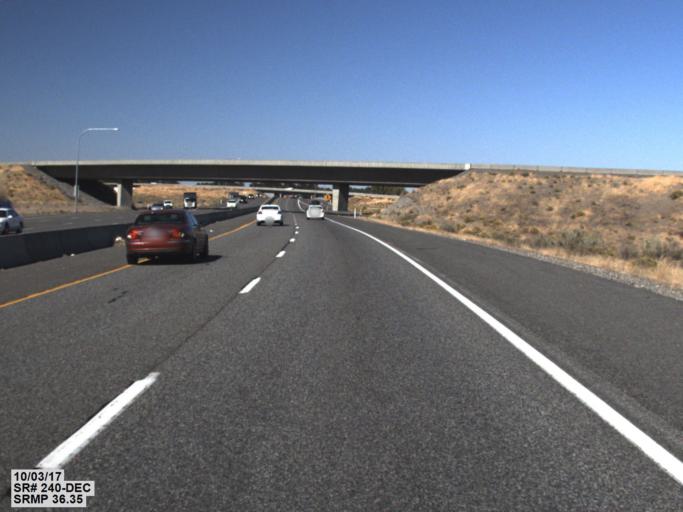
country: US
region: Washington
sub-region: Benton County
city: Richland
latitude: 46.2557
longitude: -119.2593
